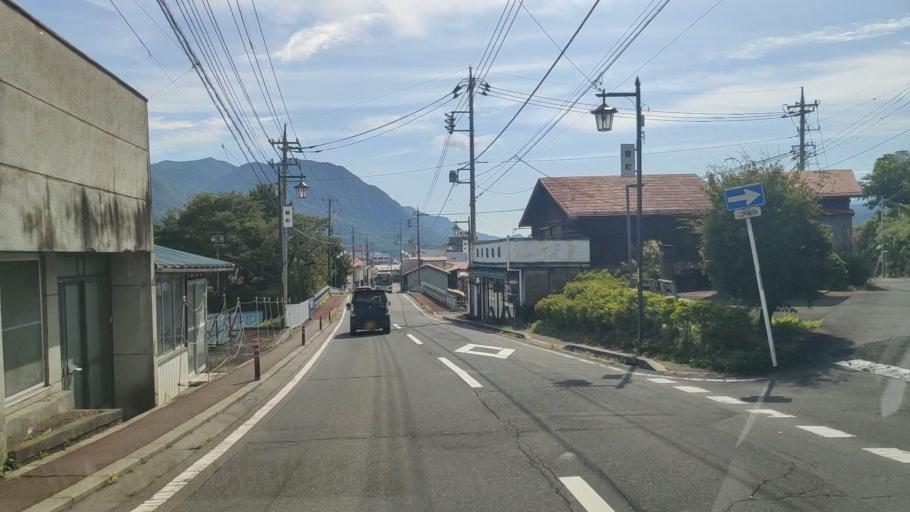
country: JP
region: Gunma
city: Nakanojomachi
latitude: 36.5877
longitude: 138.8466
